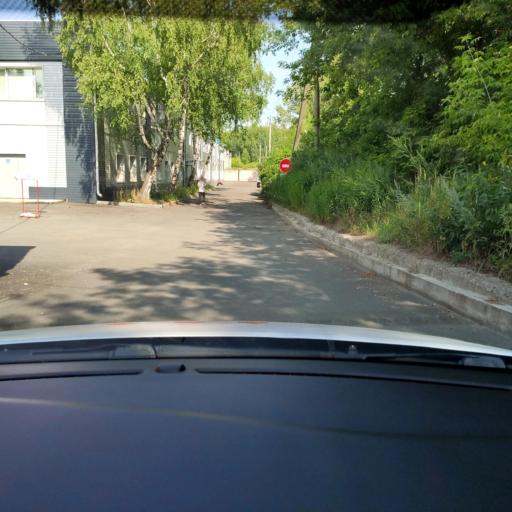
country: RU
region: Tatarstan
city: Staroye Arakchino
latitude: 55.8555
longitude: 49.0190
